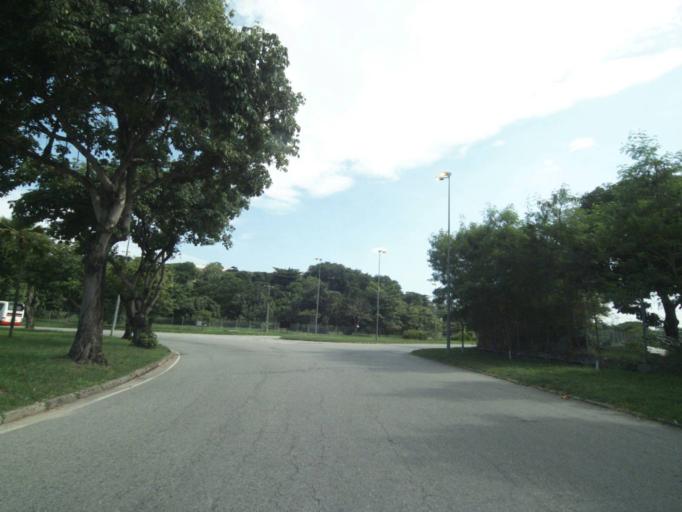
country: BR
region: Rio de Janeiro
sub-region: Rio De Janeiro
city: Rio de Janeiro
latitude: -22.8625
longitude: -43.2263
